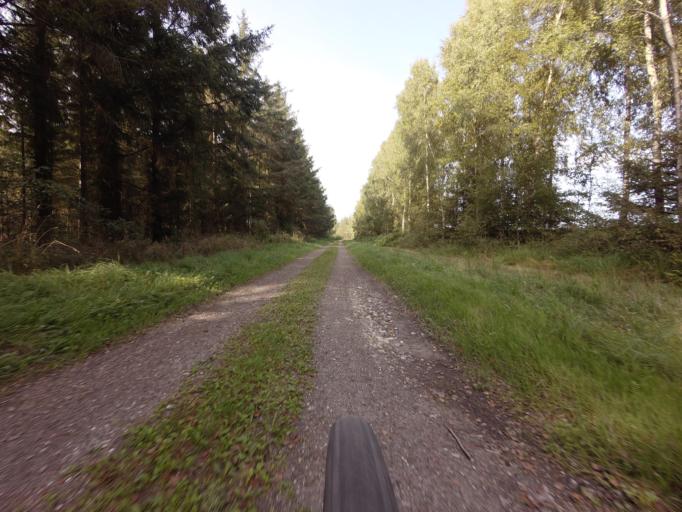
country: DK
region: Zealand
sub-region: Vordingborg Kommune
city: Praesto
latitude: 55.1508
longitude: 12.0999
